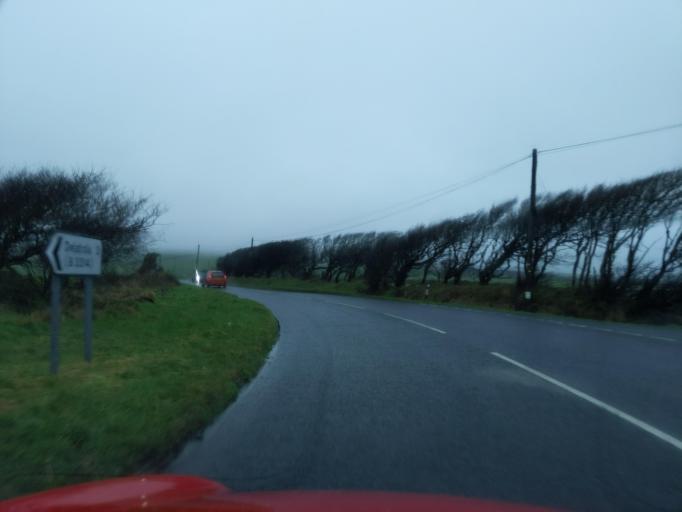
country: GB
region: England
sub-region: Cornwall
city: Camelford
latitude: 50.6446
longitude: -4.6968
